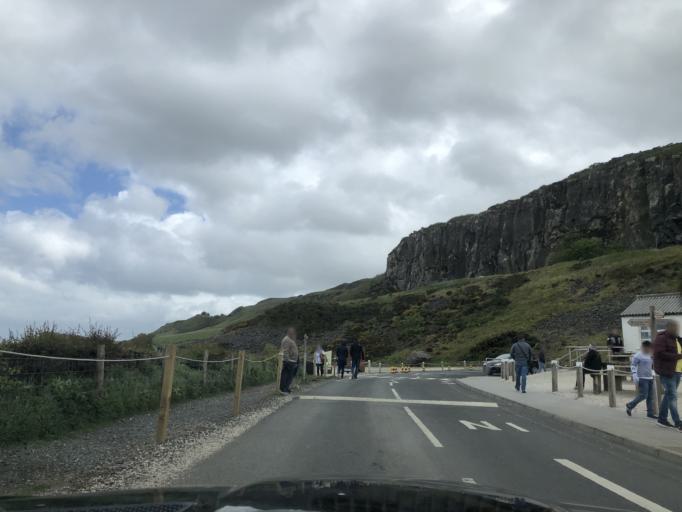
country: GB
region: Northern Ireland
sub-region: Moyle District
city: Ballycastle
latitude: 55.2393
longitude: -6.3478
